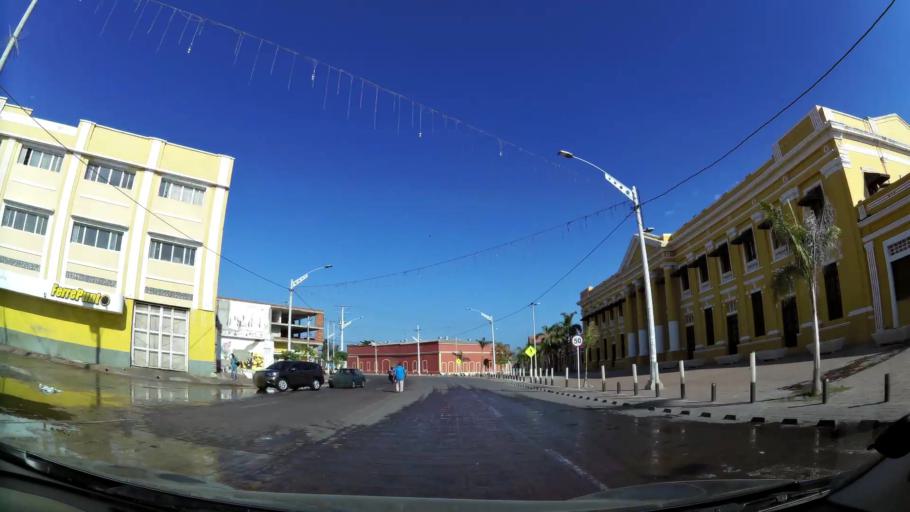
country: CO
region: Atlantico
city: Barranquilla
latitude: 10.9880
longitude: -74.7789
